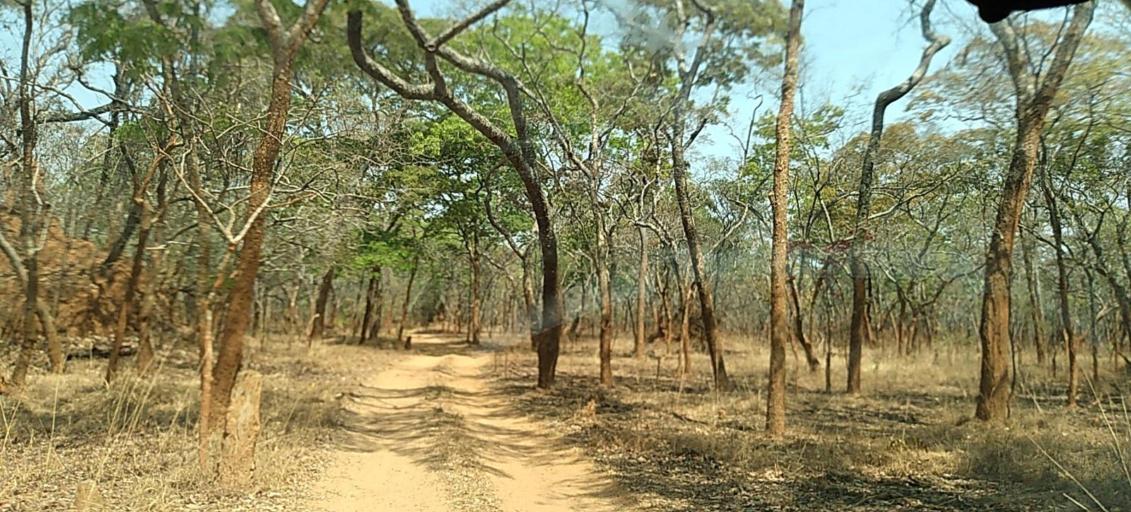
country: ZM
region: North-Western
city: Kasempa
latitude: -13.3943
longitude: 25.5818
